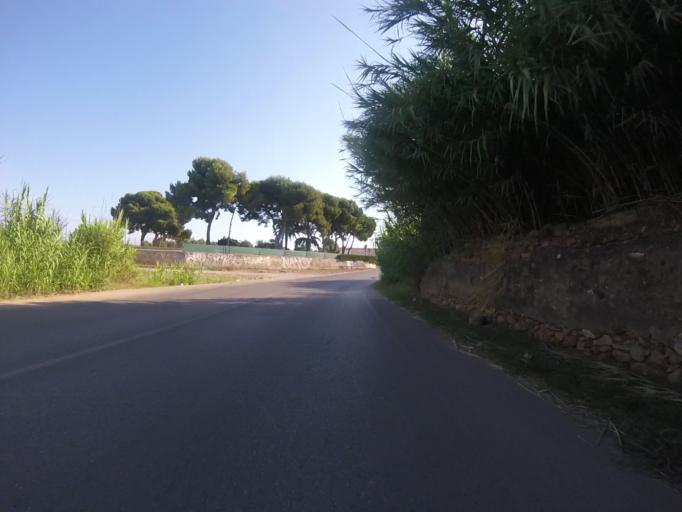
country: ES
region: Valencia
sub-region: Provincia de Castello
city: Benicarlo
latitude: 40.4038
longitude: 0.4147
